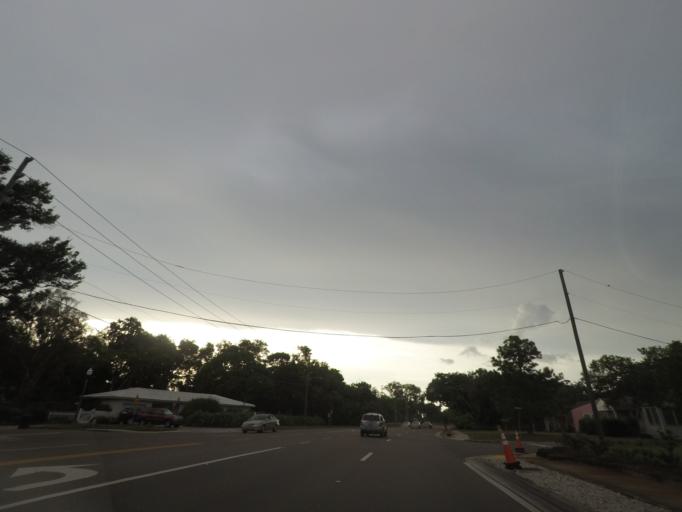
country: US
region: Florida
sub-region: Pinellas County
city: Gulfport
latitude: 27.7488
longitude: -82.7152
